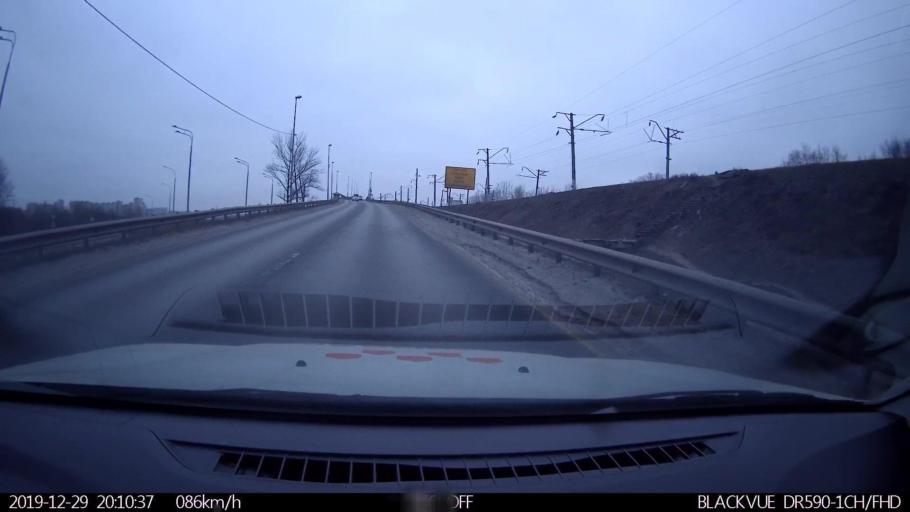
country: RU
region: Nizjnij Novgorod
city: Neklyudovo
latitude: 56.3639
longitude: 43.9342
